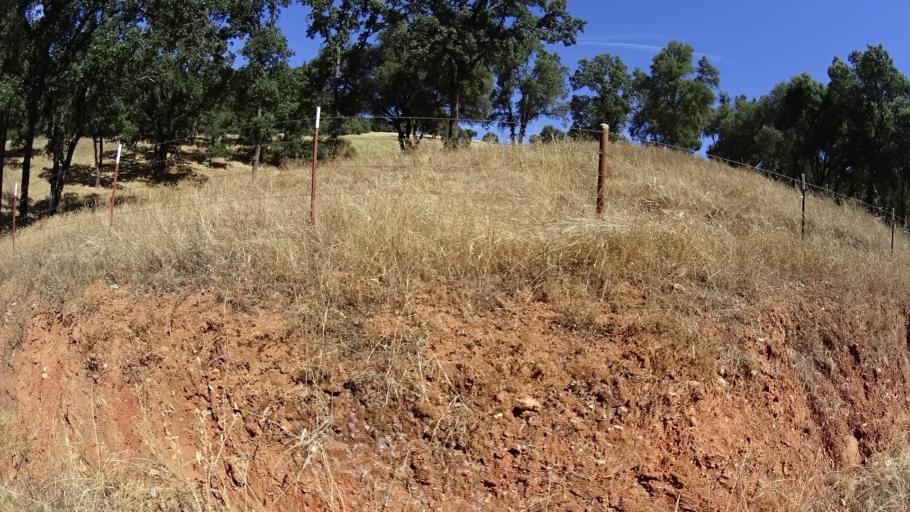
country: US
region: California
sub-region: Calaveras County
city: Angels Camp
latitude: 38.1370
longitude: -120.5569
